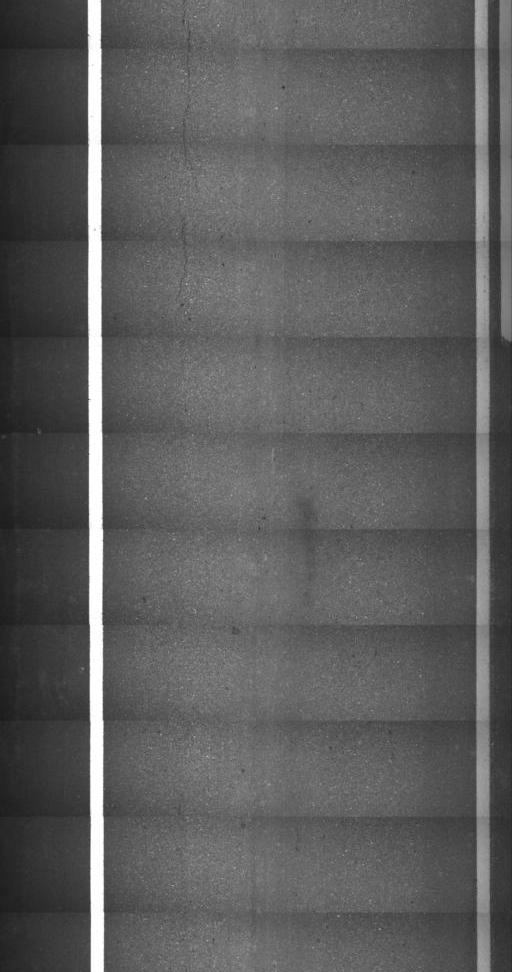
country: US
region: Vermont
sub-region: Windham County
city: Bellows Falls
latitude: 43.0838
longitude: -72.4408
